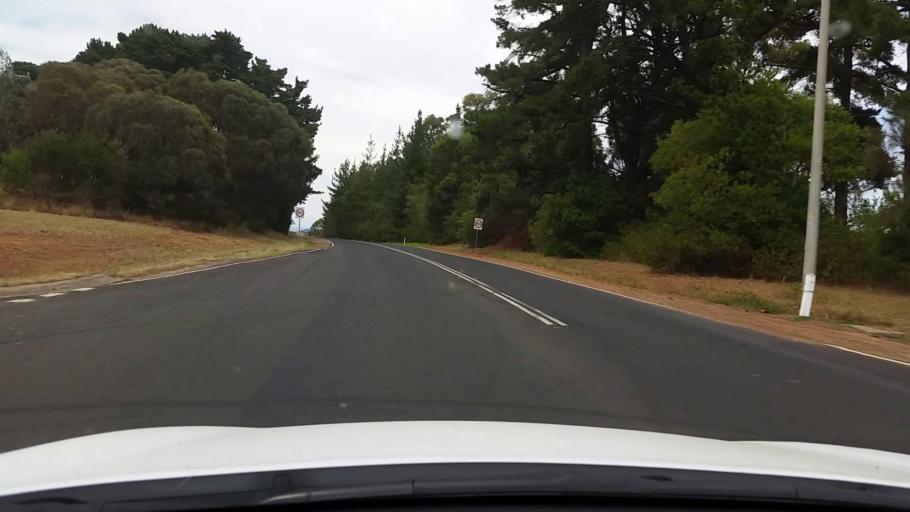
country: AU
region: Victoria
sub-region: Mornington Peninsula
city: Merricks
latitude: -38.4200
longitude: 145.0441
